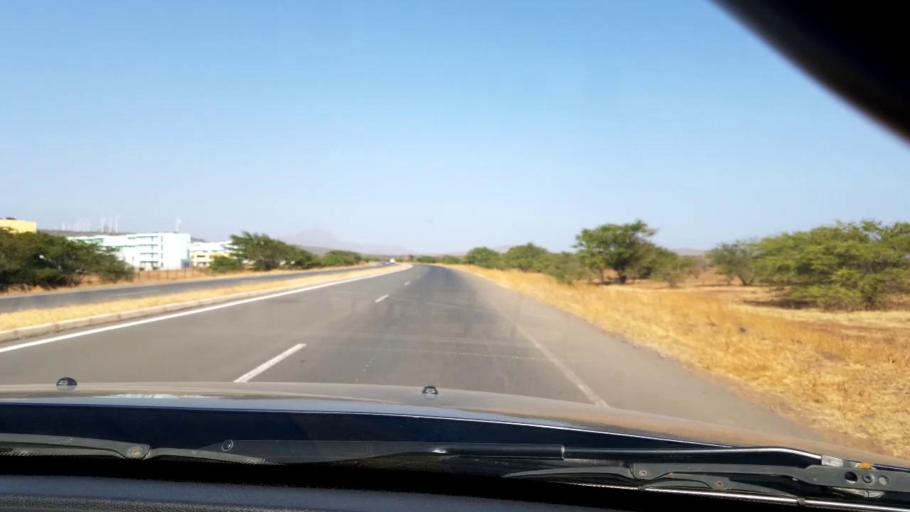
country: CV
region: Praia
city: Praia
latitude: 14.9490
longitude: -23.4910
